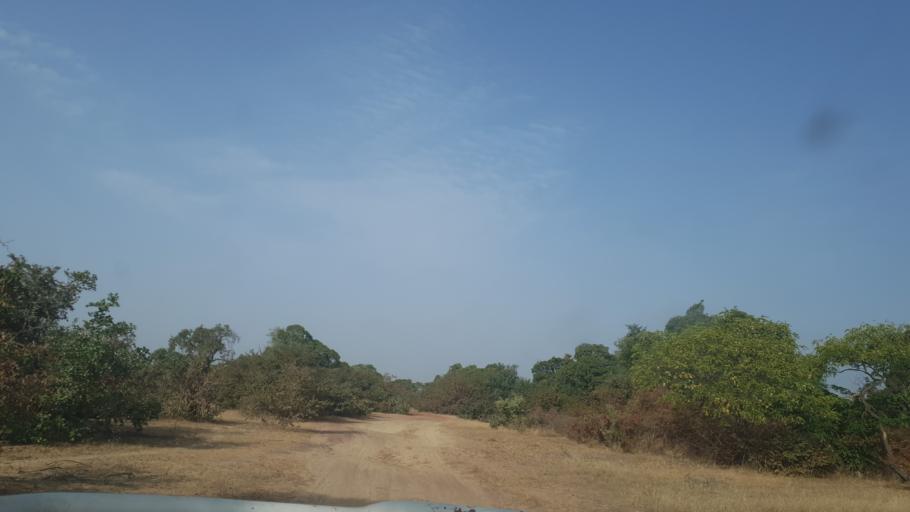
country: ML
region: Segou
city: Baroueli
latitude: 13.3614
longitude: -6.9212
